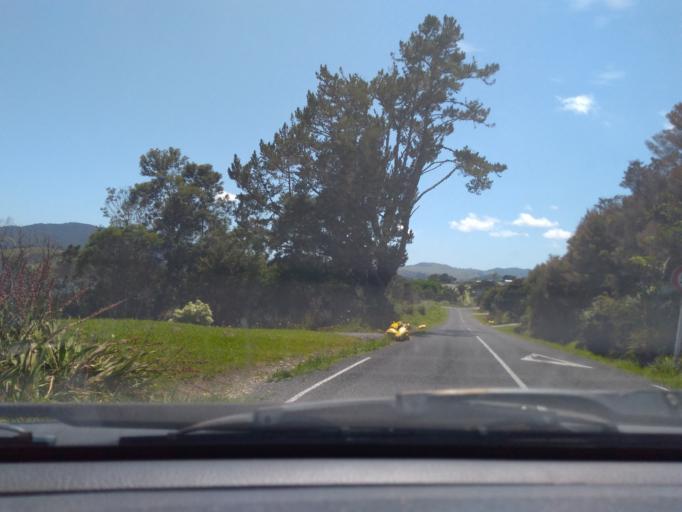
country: NZ
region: Northland
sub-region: Far North District
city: Taipa
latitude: -34.9943
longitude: 173.5259
